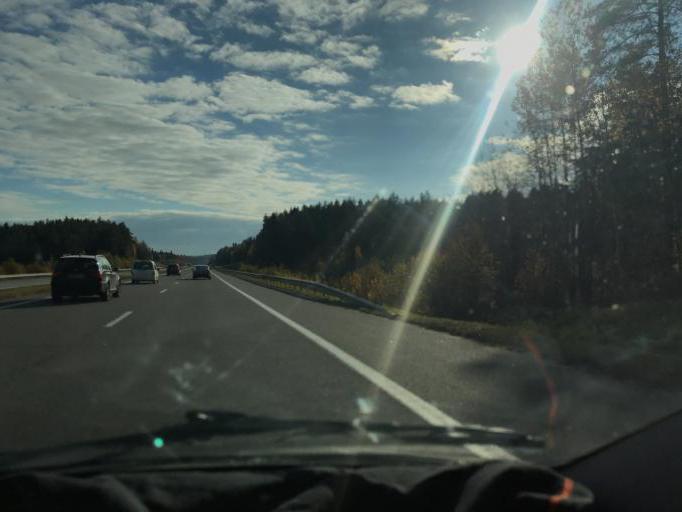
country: BY
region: Minsk
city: Lahoysk
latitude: 54.1398
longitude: 27.8090
